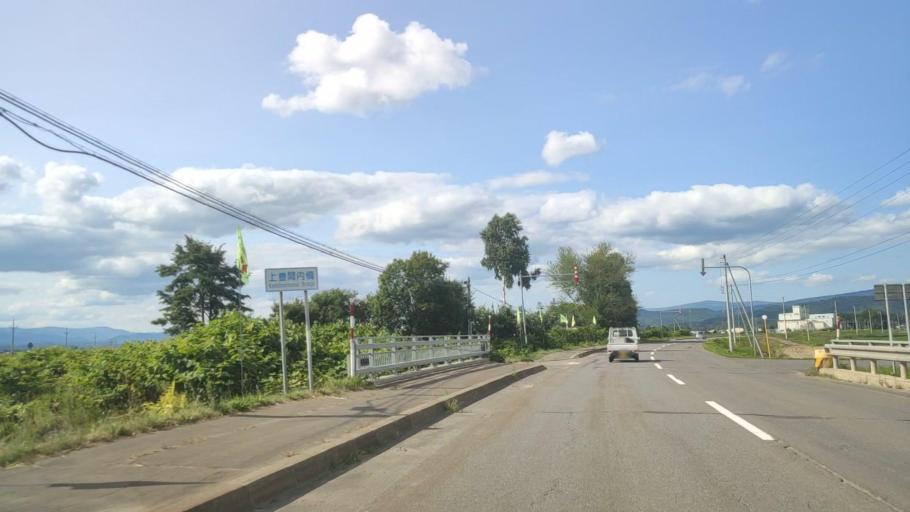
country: JP
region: Hokkaido
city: Nayoro
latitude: 44.4272
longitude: 142.3998
